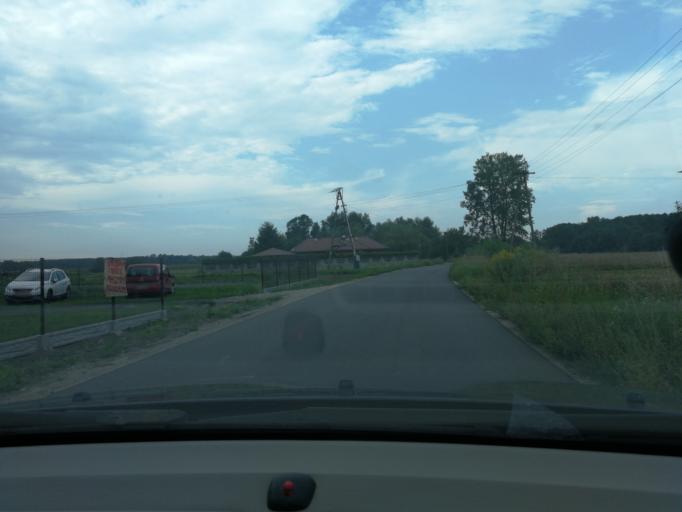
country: PL
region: Masovian Voivodeship
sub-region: Powiat warszawski zachodni
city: Bieniewice
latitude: 52.1074
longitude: 20.5549
